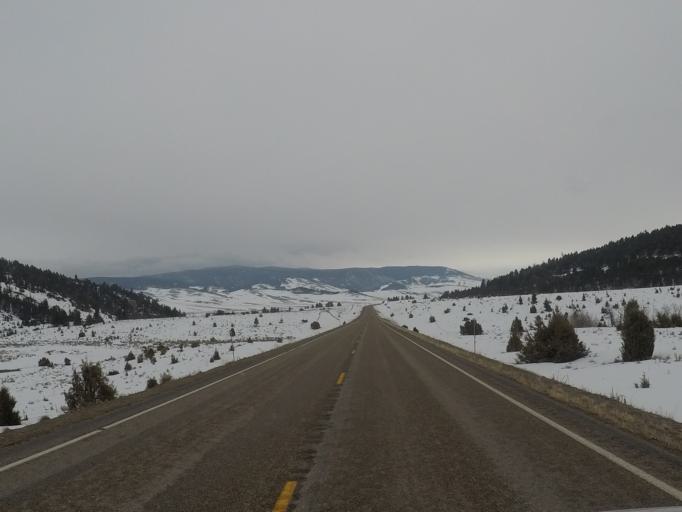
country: US
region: Montana
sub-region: Meagher County
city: White Sulphur Springs
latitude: 46.6140
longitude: -110.8440
